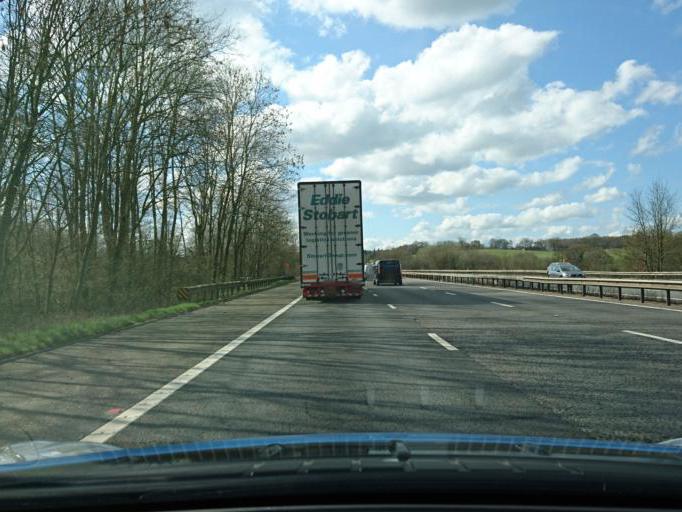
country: GB
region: England
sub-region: West Berkshire
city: Pangbourne
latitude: 51.4584
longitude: -1.0948
